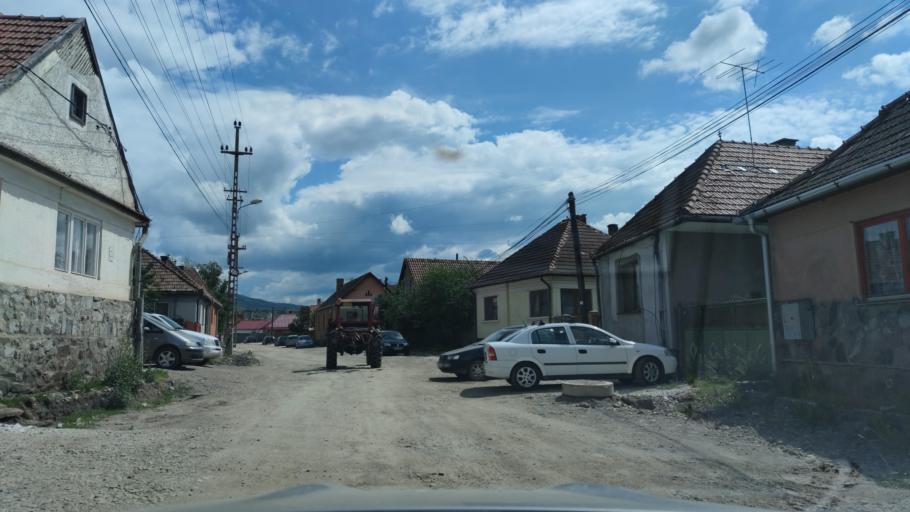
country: RO
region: Harghita
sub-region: Municipiul Gheorgheni
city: Gheorgheni
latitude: 46.7172
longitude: 25.5921
